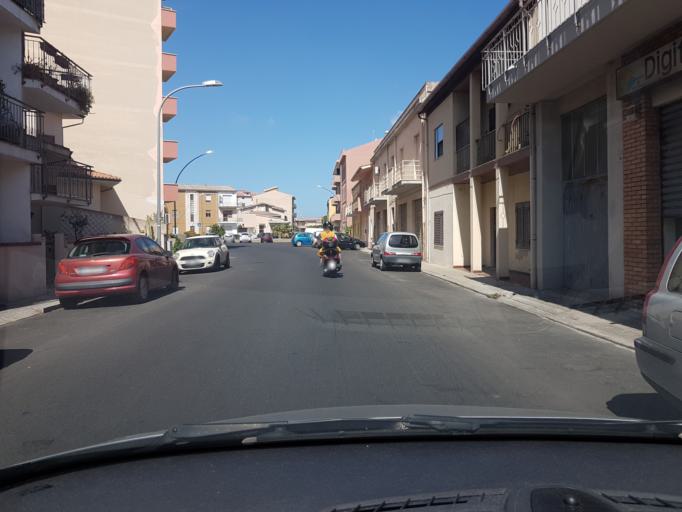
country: IT
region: Sardinia
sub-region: Provincia di Oristano
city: Oristano
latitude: 39.9096
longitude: 8.5933
